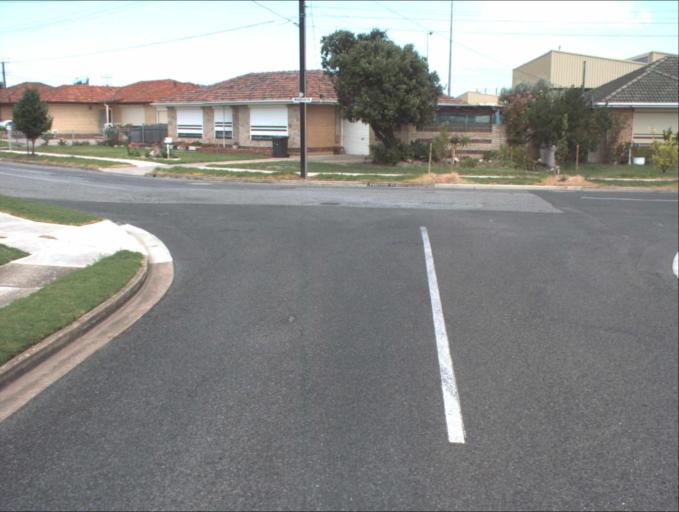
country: AU
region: South Australia
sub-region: Charles Sturt
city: Woodville
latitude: -34.8793
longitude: 138.5601
